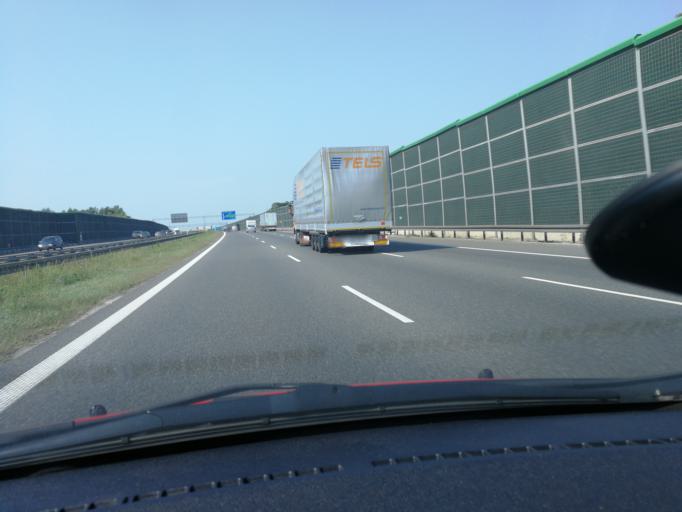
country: PL
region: Masovian Voivodeship
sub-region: Powiat warszawski zachodni
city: Ozarow Mazowiecki
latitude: 52.1931
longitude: 20.8071
